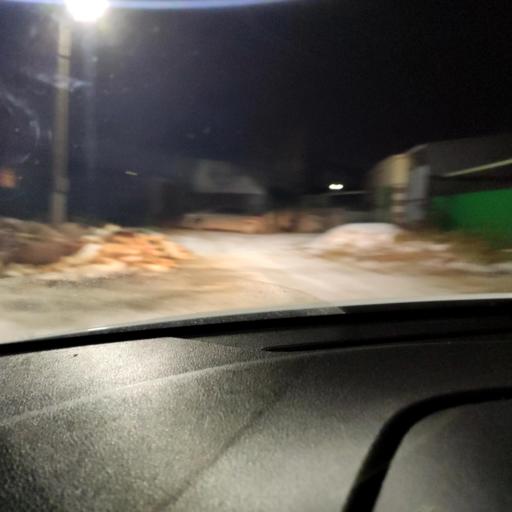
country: RU
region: Tatarstan
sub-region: Gorod Kazan'
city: Kazan
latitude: 55.7184
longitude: 49.0940
